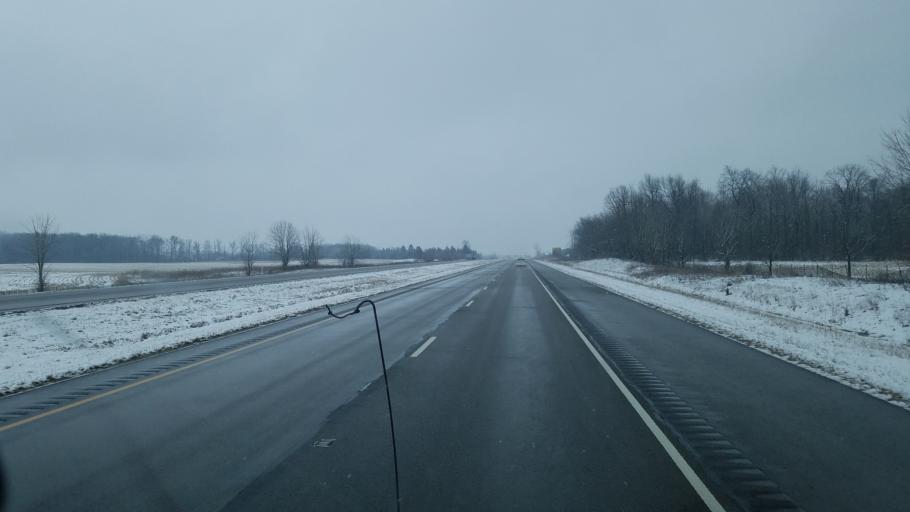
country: US
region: Indiana
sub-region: Delaware County
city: Muncie
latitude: 40.2283
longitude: -85.3467
